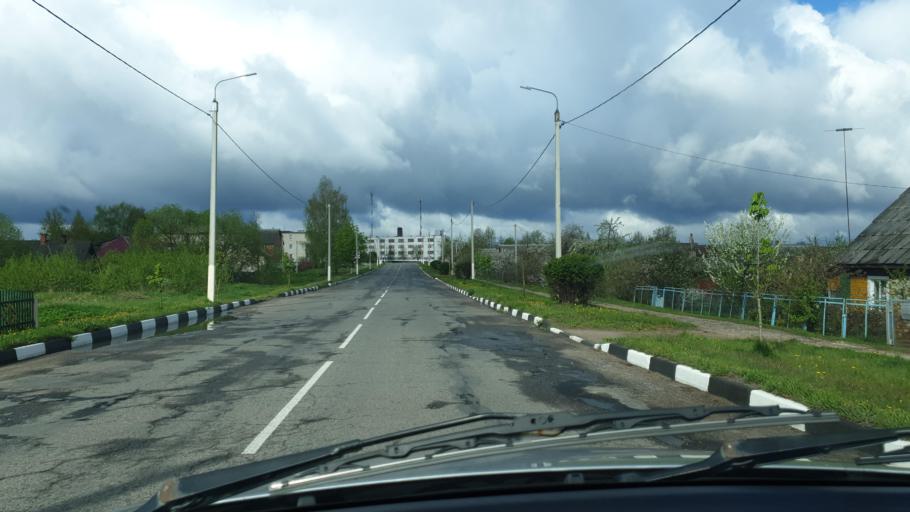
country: BY
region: Vitebsk
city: Lyepyel'
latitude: 54.8757
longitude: 28.6841
